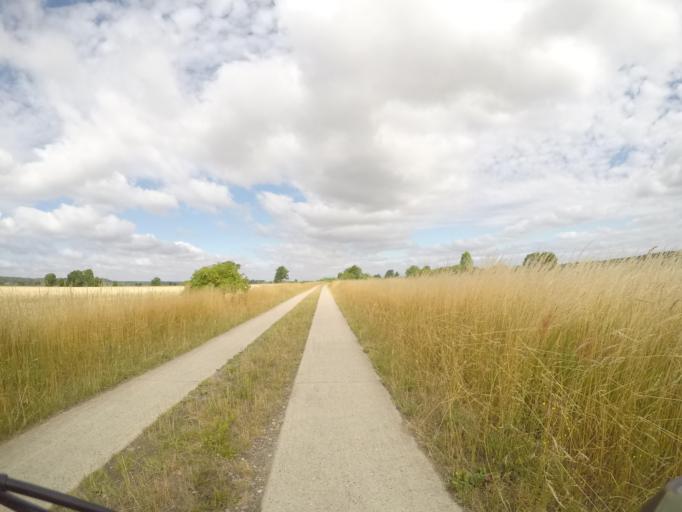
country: DE
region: Lower Saxony
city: Hitzacker
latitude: 53.1759
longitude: 11.0458
